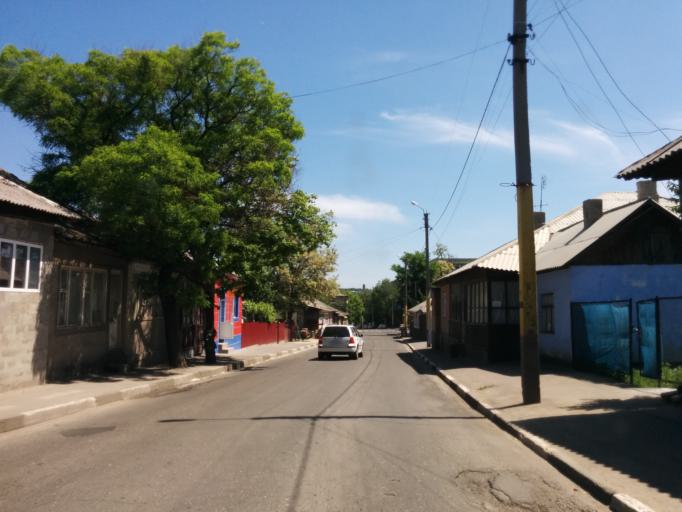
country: MD
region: Raionul Soroca
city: Soroca
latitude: 48.1623
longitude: 28.2998
